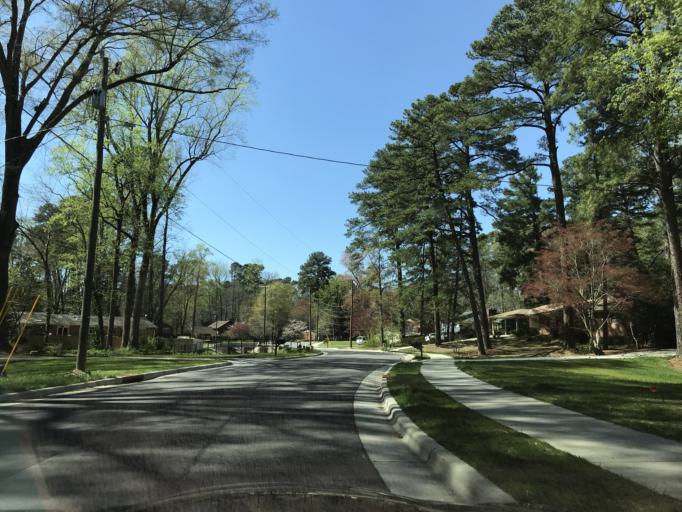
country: US
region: North Carolina
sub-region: Wake County
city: West Raleigh
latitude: 35.7704
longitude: -78.7060
